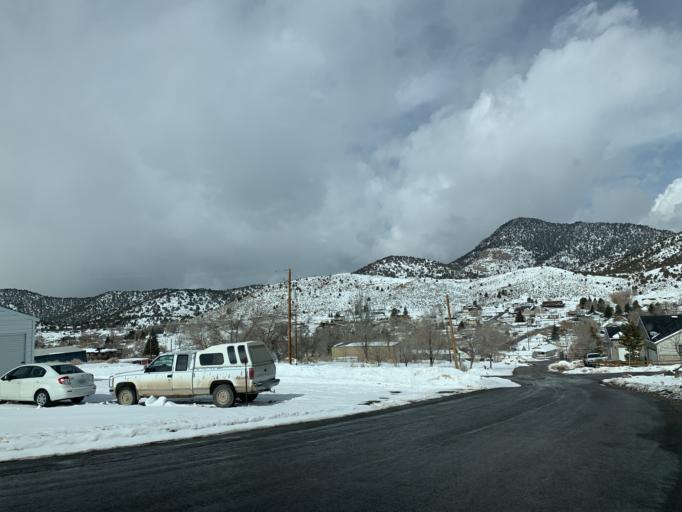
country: US
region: Utah
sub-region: Utah County
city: Genola
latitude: 39.9535
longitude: -112.1130
